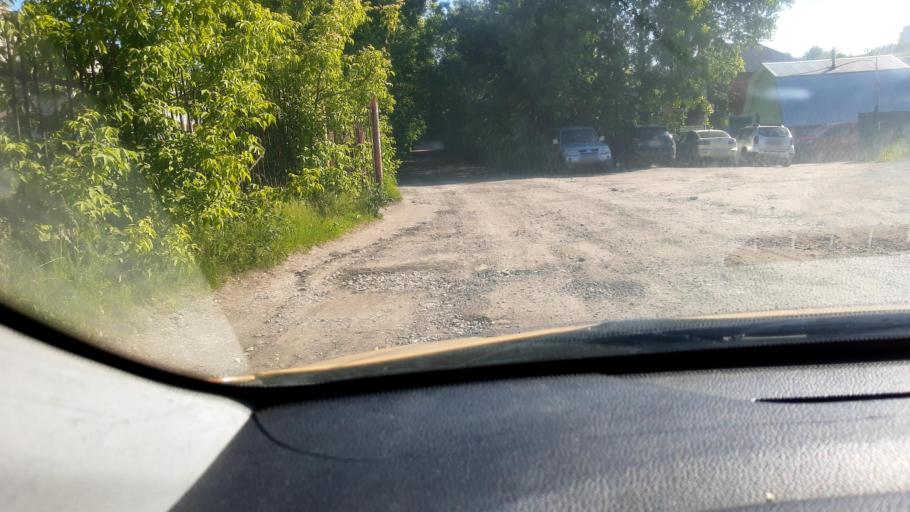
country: RU
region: Moskovskaya
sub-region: Podol'skiy Rayon
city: Podol'sk
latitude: 55.4555
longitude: 37.5598
